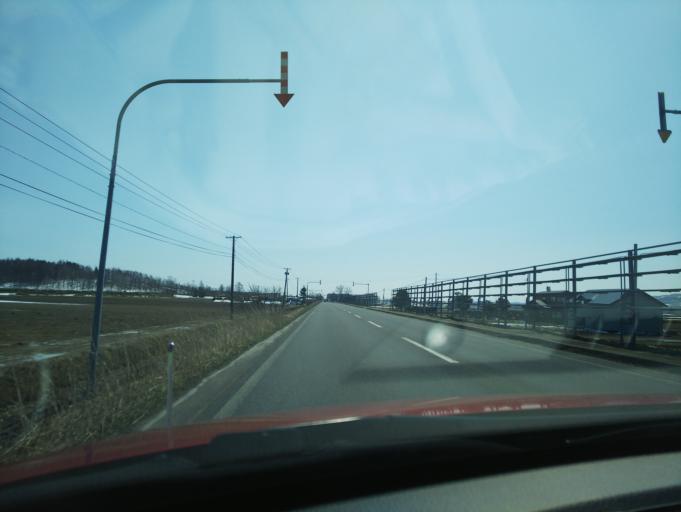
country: JP
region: Hokkaido
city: Nayoro
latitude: 44.2645
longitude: 142.3946
